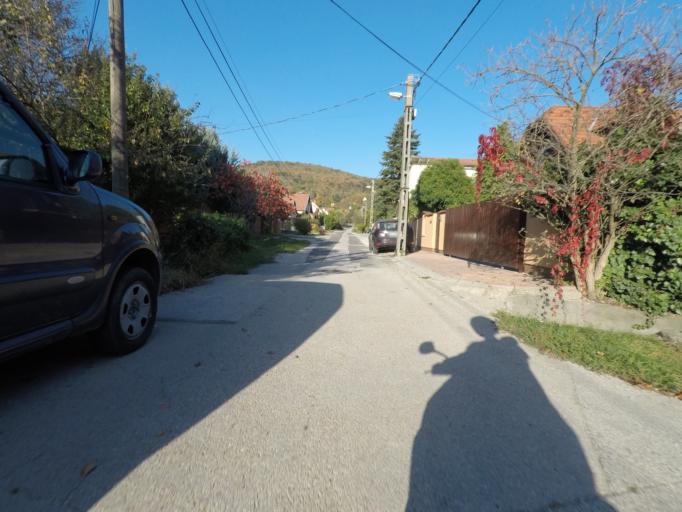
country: HU
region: Pest
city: Nagykovacsi
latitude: 47.6516
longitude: 19.0000
